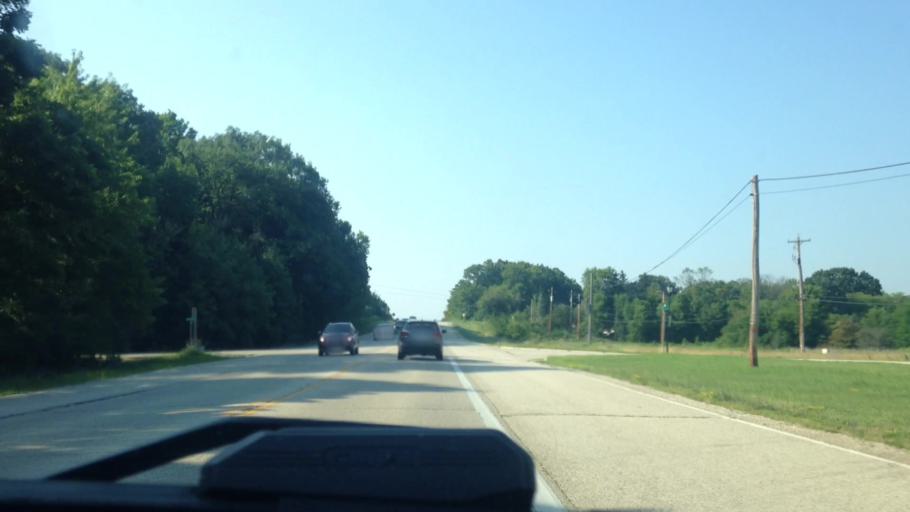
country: US
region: Wisconsin
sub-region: Waukesha County
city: Merton
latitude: 43.2026
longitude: -88.2616
